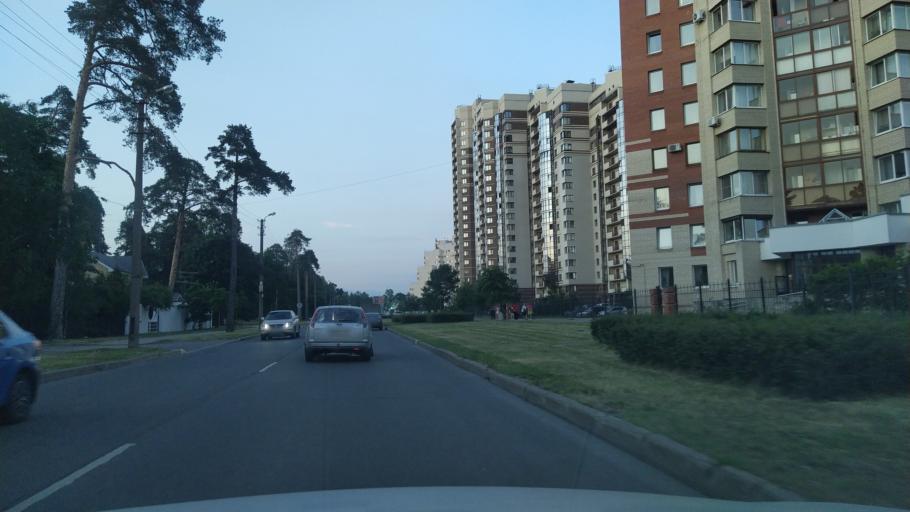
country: RU
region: St.-Petersburg
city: Sestroretsk
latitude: 60.0912
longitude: 29.9511
